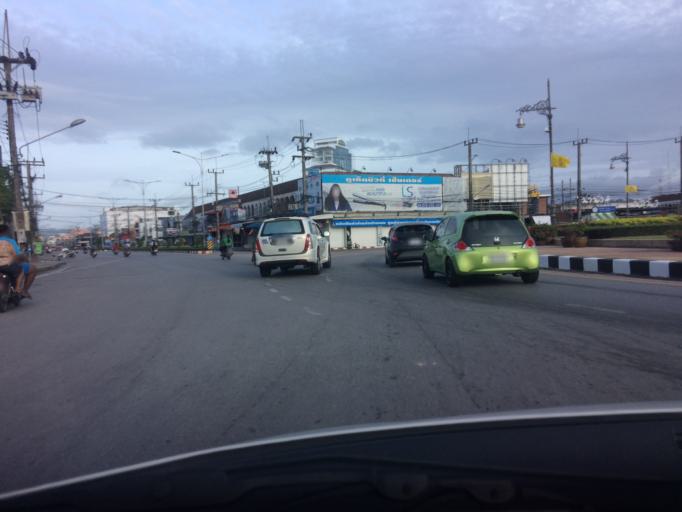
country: TH
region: Phuket
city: Ban Talat Yai
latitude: 7.8786
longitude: 98.3985
